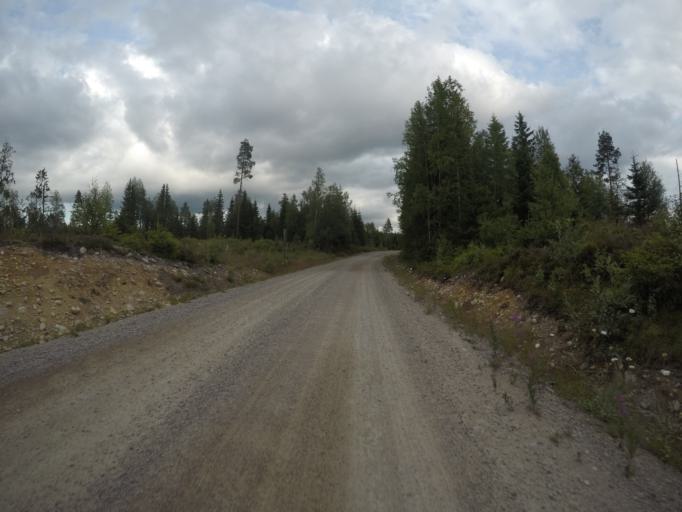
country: SE
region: Vaermland
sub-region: Filipstads Kommun
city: Lesjofors
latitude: 60.1755
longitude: 14.4056
